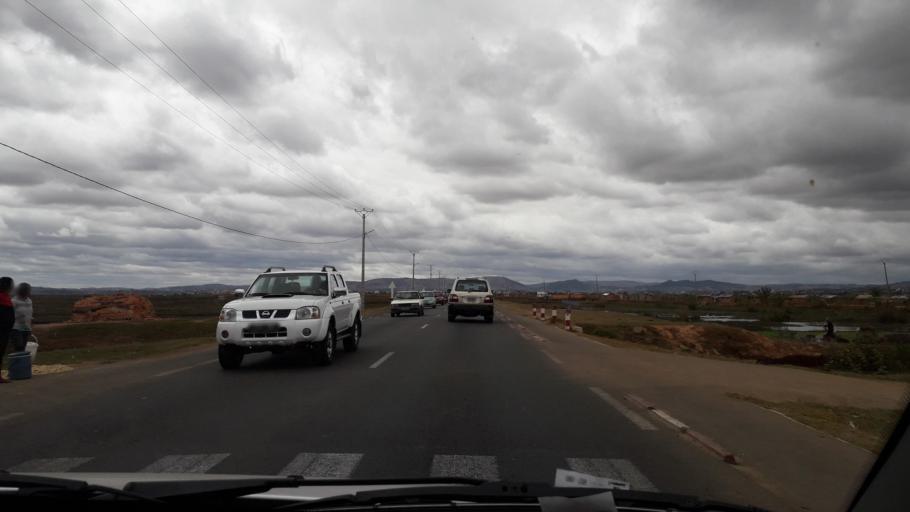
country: MG
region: Analamanga
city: Antananarivo
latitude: -18.8479
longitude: 47.5132
